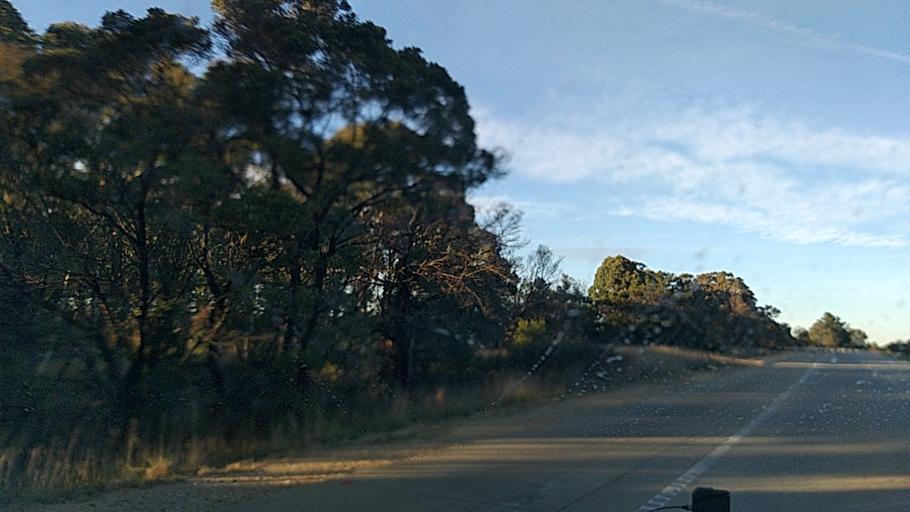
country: AU
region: New South Wales
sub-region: Yass Valley
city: Gundaroo
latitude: -35.1318
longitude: 149.3411
